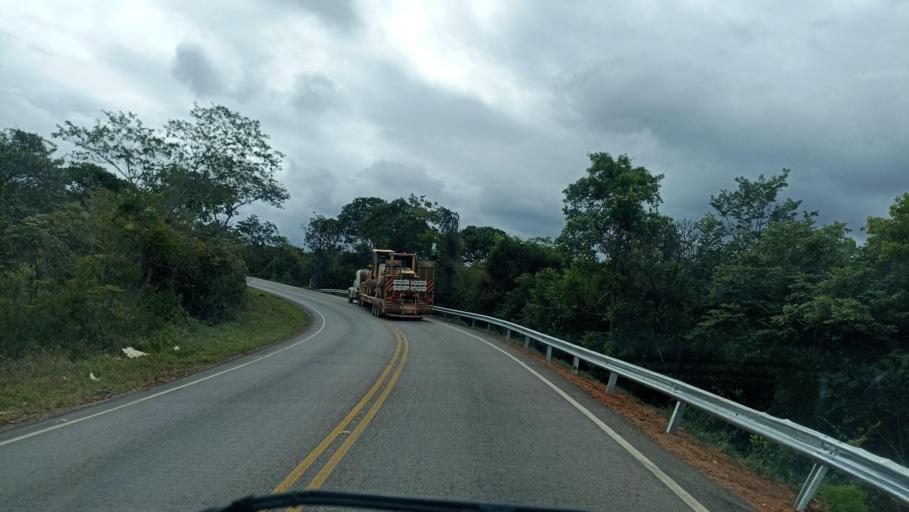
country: BR
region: Bahia
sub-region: Andarai
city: Vera Cruz
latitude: -12.9309
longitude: -41.2439
